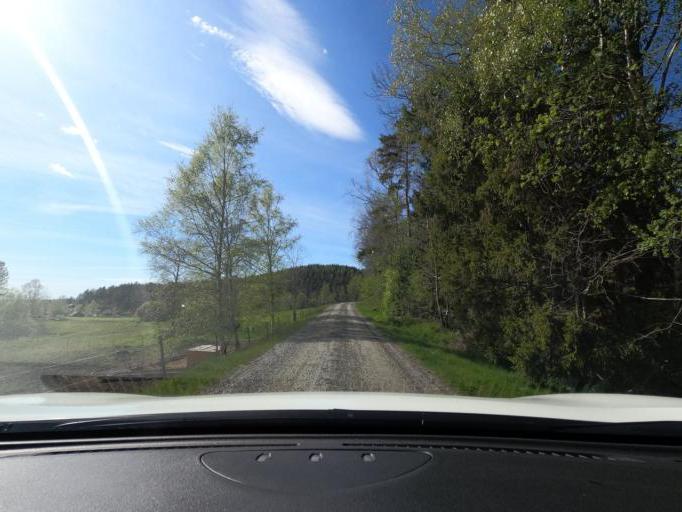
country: SE
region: Vaestra Goetaland
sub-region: Harryda Kommun
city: Ravlanda
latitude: 57.5875
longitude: 12.4905
